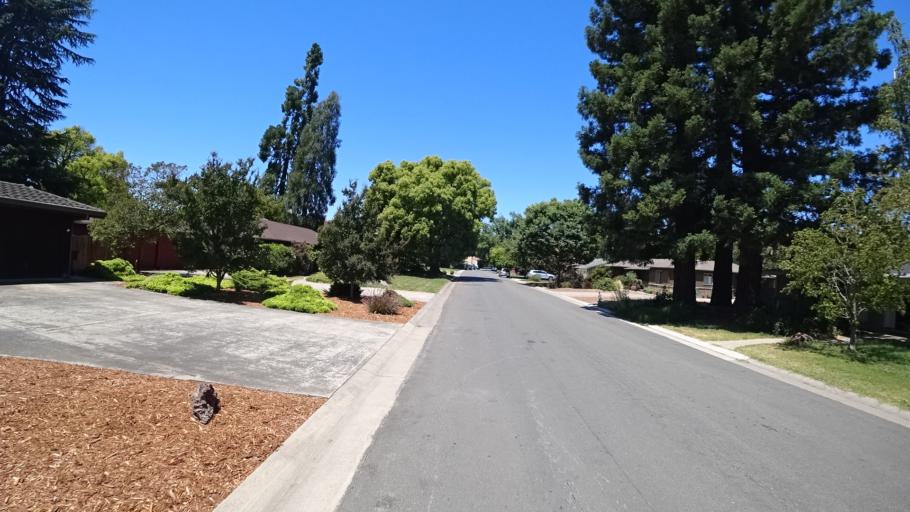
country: US
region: California
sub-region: Yolo County
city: West Sacramento
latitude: 38.5287
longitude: -121.5220
